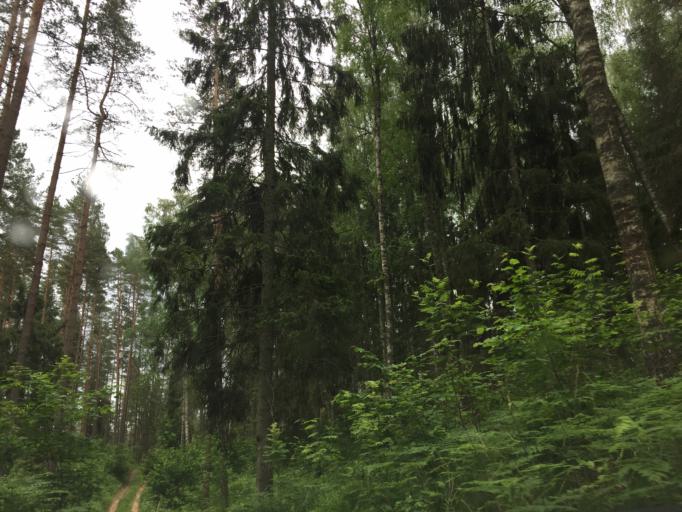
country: LV
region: Tukuma Rajons
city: Tukums
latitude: 57.0293
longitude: 23.0764
